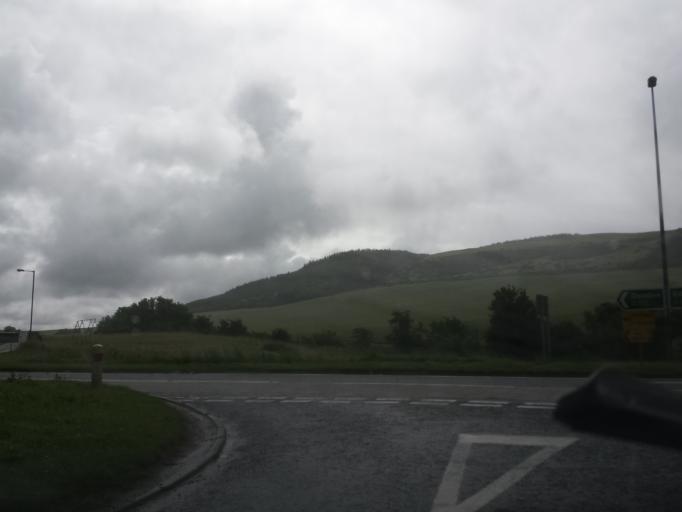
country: GB
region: Scotland
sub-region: Fife
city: Ladybank
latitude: 56.3445
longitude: -3.0963
